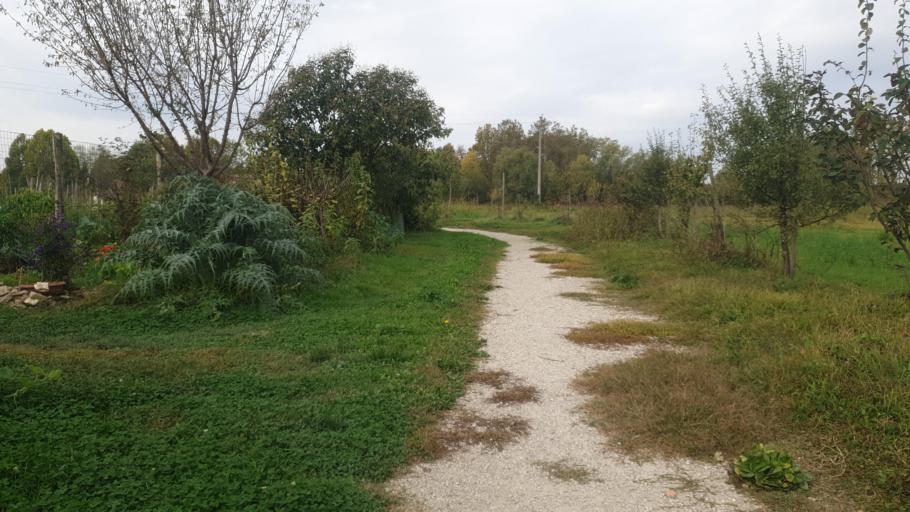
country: IT
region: Veneto
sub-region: Provincia di Padova
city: Mandriola-Sant'Agostino
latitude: 45.3874
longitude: 11.8546
